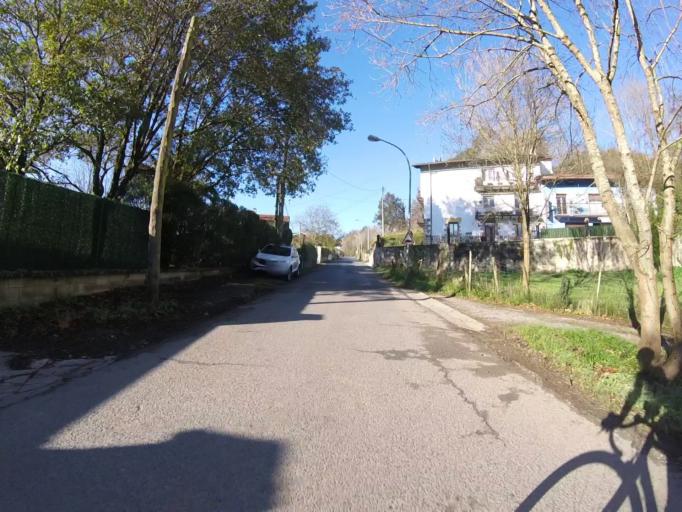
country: ES
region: Basque Country
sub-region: Provincia de Guipuzcoa
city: Usurbil
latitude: 43.2713
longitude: -2.0679
